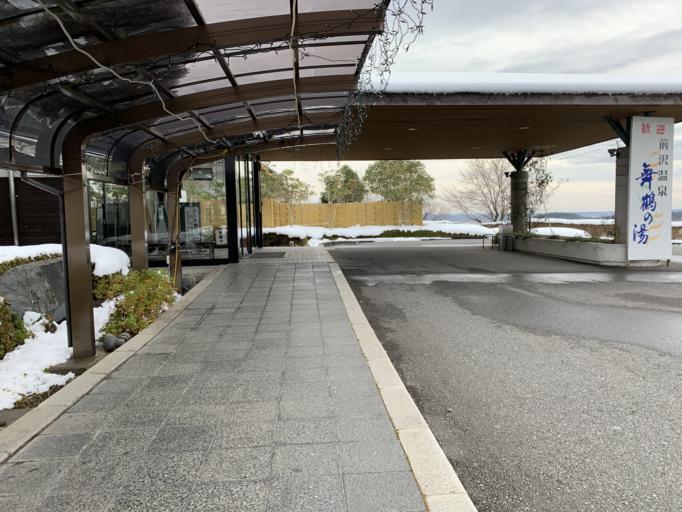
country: JP
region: Iwate
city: Mizusawa
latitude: 39.0300
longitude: 141.1084
